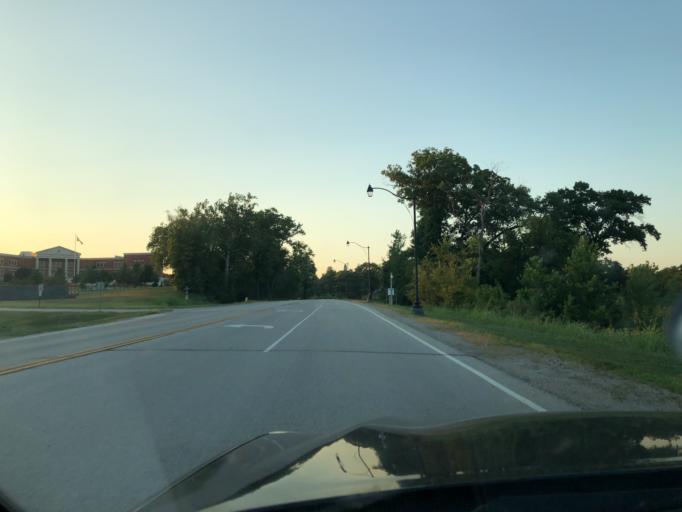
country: US
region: Kansas
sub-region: Leavenworth County
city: Leavenworth
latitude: 39.3416
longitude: -94.9134
